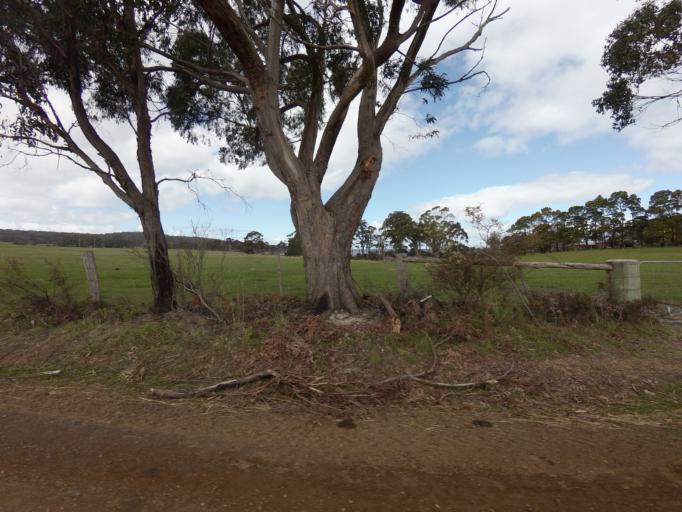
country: AU
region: Tasmania
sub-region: Huon Valley
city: Geeveston
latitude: -43.4327
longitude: 146.9887
